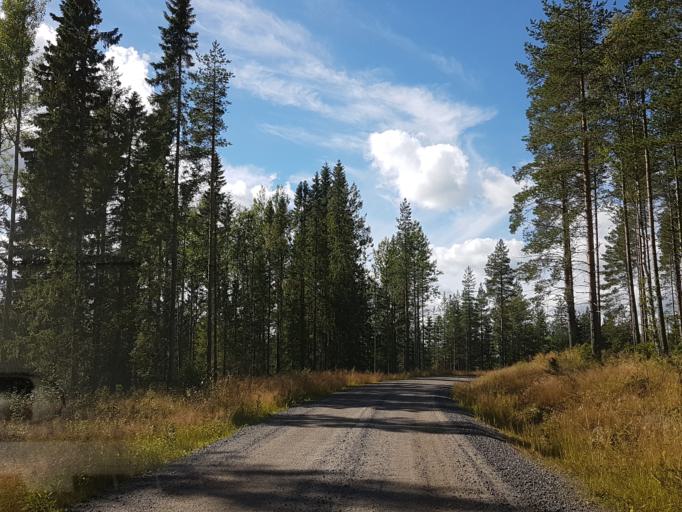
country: SE
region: Vaesterbotten
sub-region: Skelleftea Kommun
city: Burtraesk
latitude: 64.2728
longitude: 20.4851
